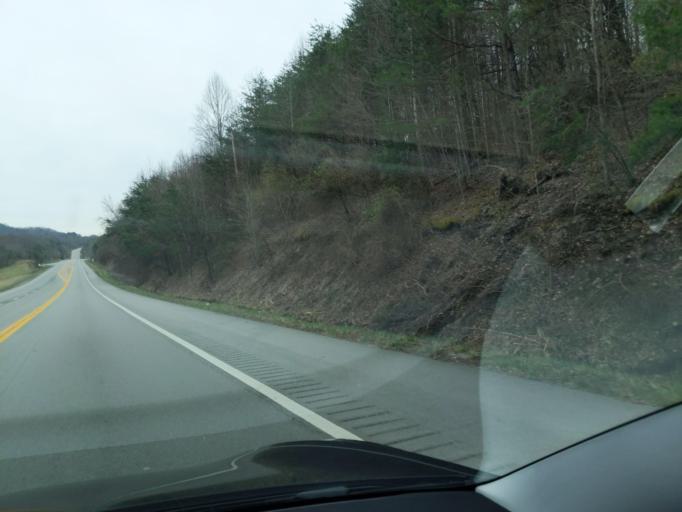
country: US
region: Kentucky
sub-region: Whitley County
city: Corbin
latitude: 36.9171
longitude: -84.0950
